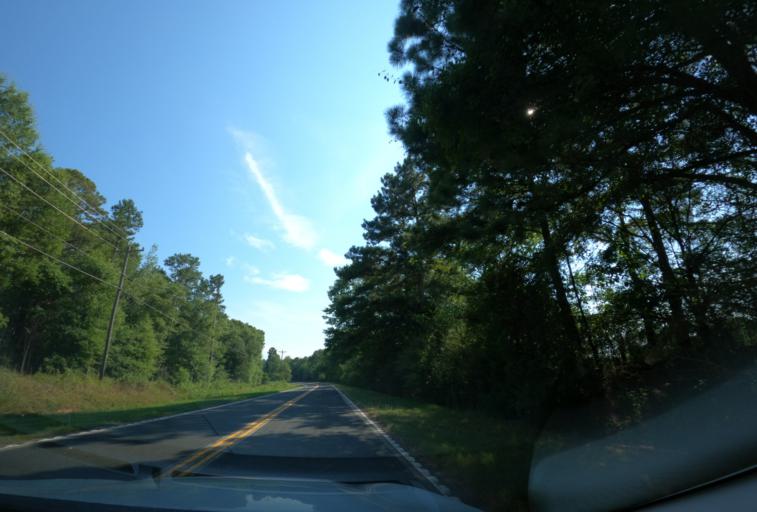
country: US
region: South Carolina
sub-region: Anderson County
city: Belton
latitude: 34.4549
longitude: -82.5470
